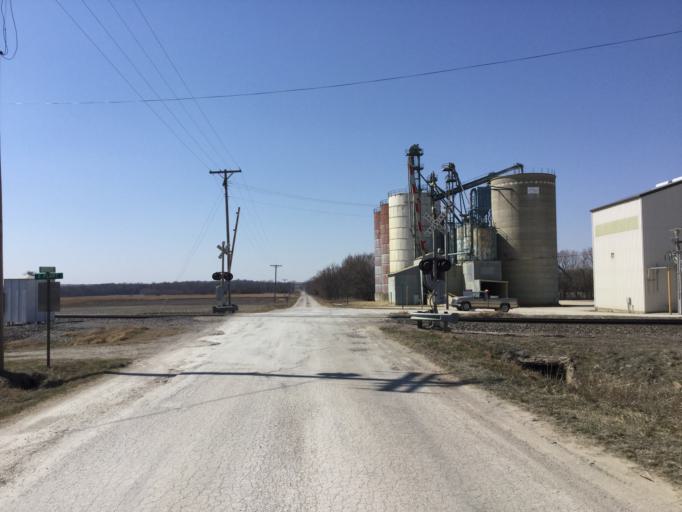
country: US
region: Kansas
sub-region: Woodson County
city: Yates Center
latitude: 37.7082
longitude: -95.7037
